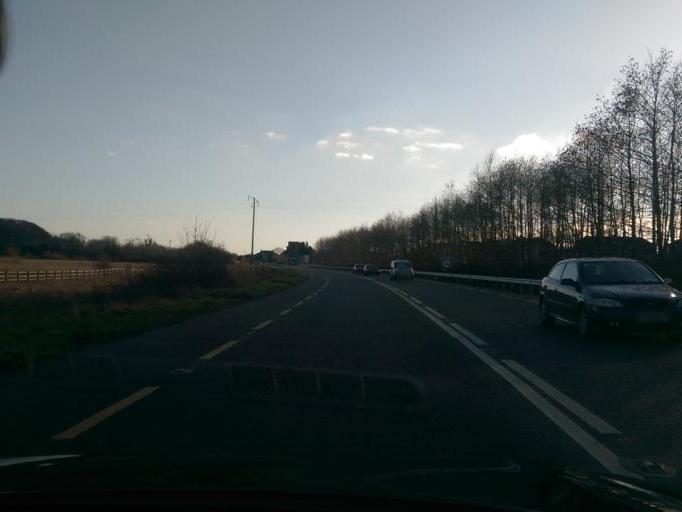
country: IE
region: Connaught
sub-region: County Galway
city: Oranmore
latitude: 53.2663
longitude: -8.9216
